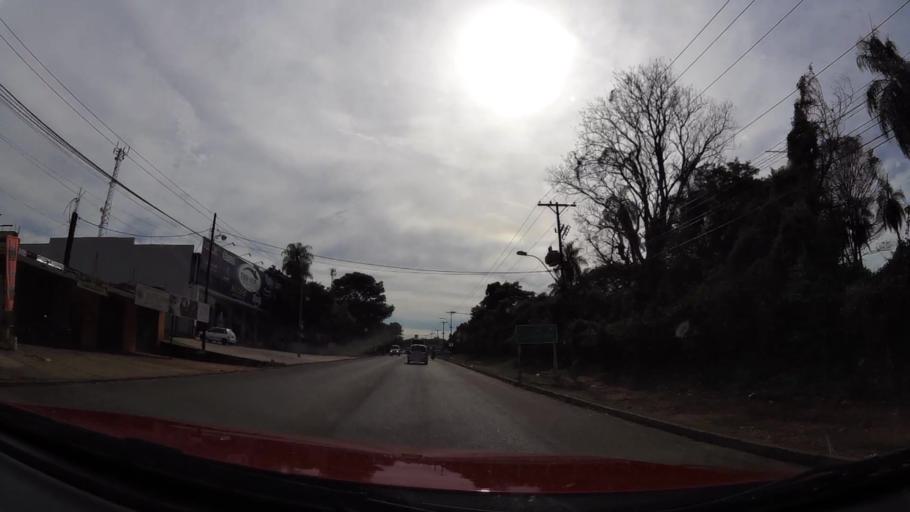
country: PY
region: Central
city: Limpio
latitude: -25.1675
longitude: -57.4719
